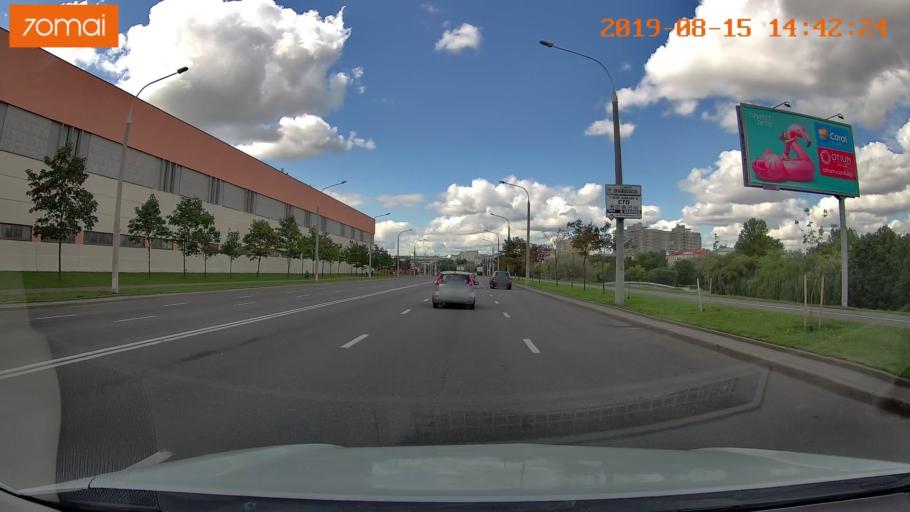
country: BY
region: Minsk
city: Minsk
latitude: 53.8911
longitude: 27.5759
